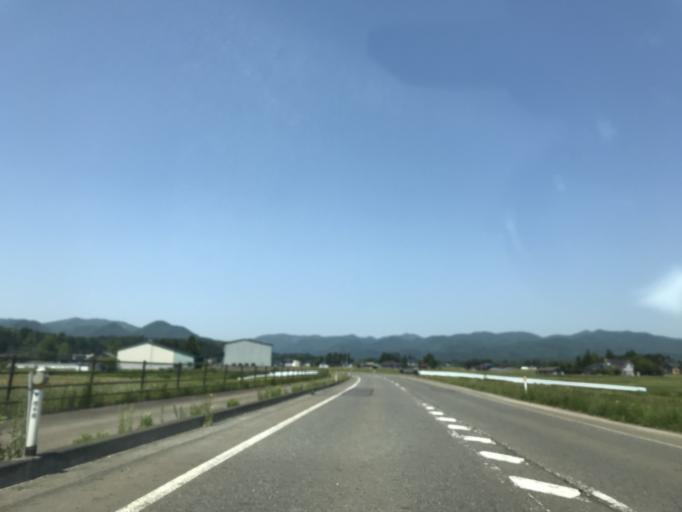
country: JP
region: Iwate
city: Kitakami
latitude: 39.2836
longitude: 141.0185
